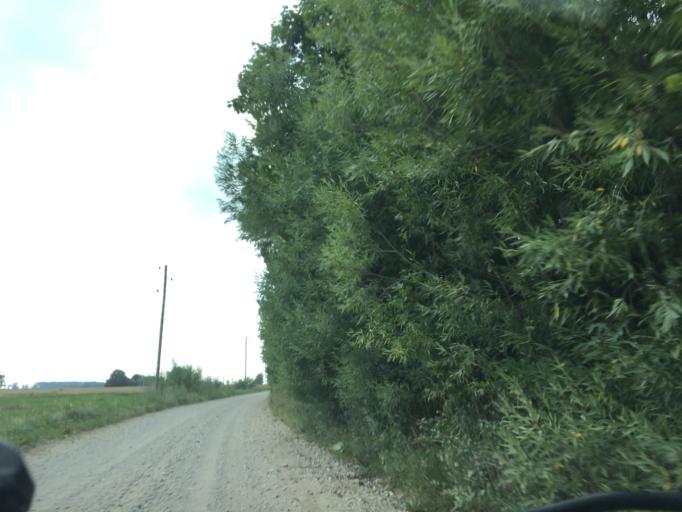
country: LT
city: Zagare
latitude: 56.3483
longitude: 23.1467
